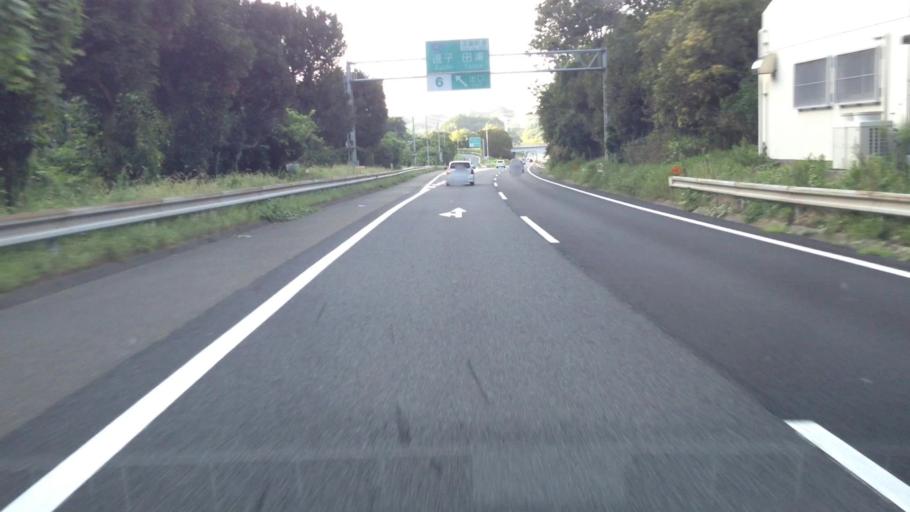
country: JP
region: Kanagawa
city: Zushi
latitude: 35.2878
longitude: 139.6210
